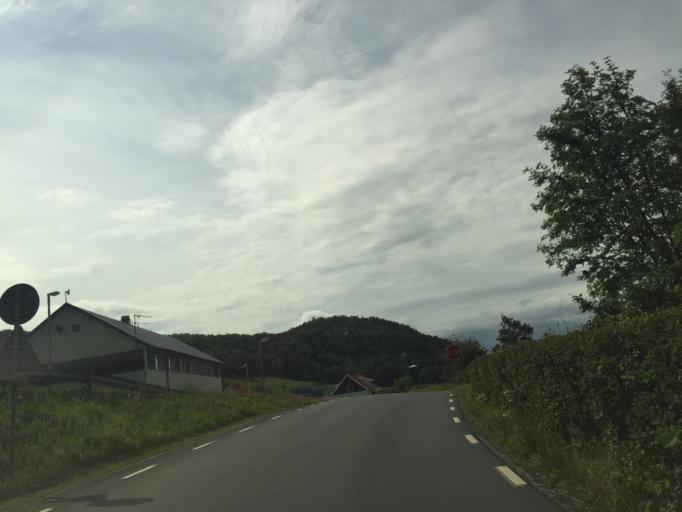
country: SE
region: Joenkoeping
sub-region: Jonkopings Kommun
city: Kaxholmen
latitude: 57.8376
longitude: 14.2727
